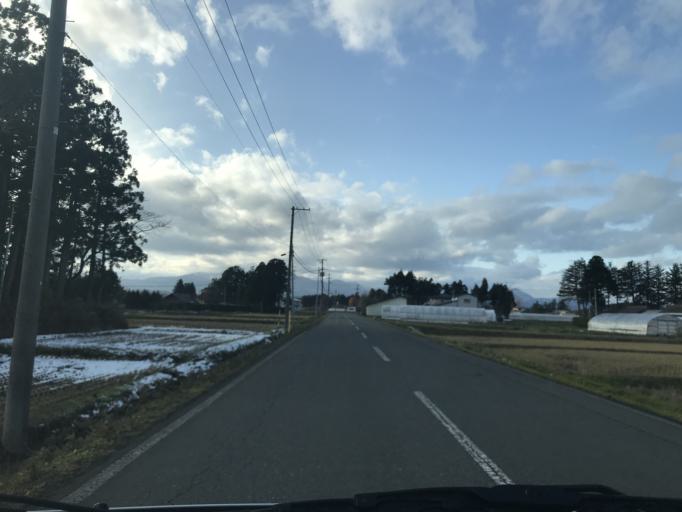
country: JP
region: Iwate
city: Mizusawa
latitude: 39.1875
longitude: 141.0988
